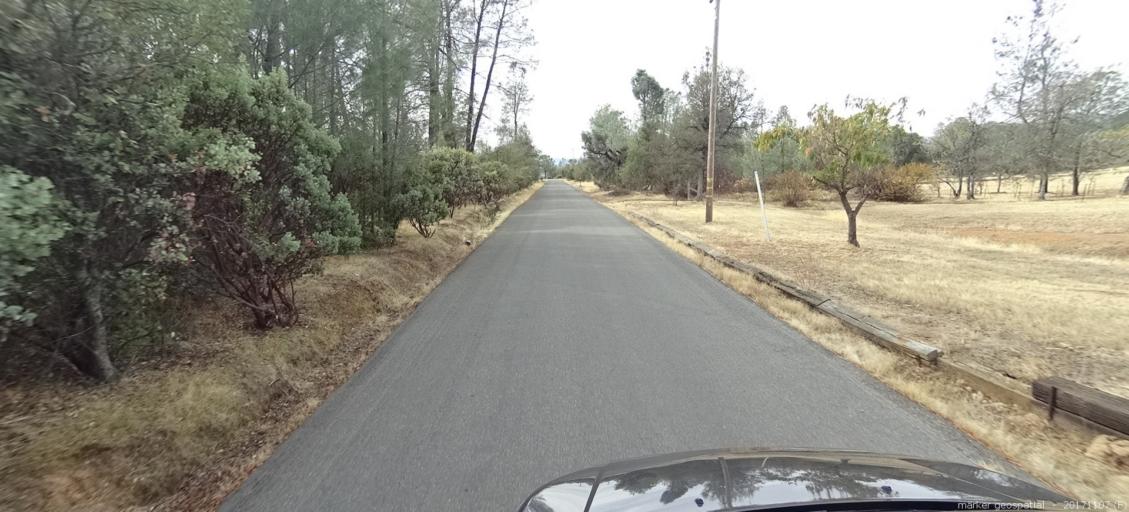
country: US
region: California
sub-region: Shasta County
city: Shasta
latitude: 40.4773
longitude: -122.4924
